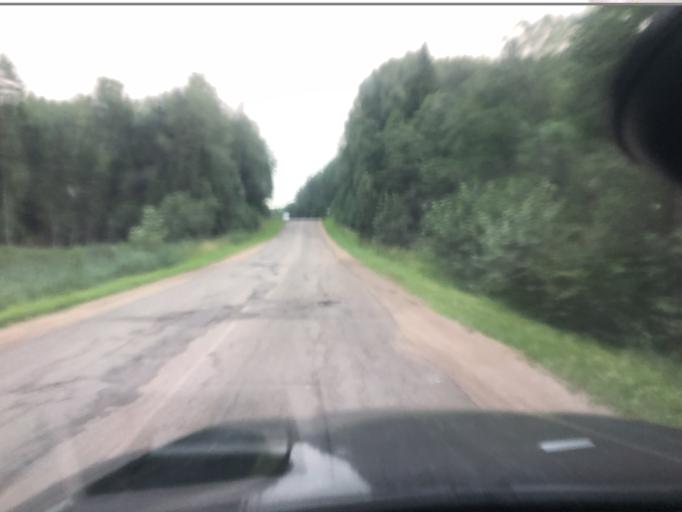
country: RU
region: Jaroslavl
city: Petrovsk
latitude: 56.9995
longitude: 39.0864
